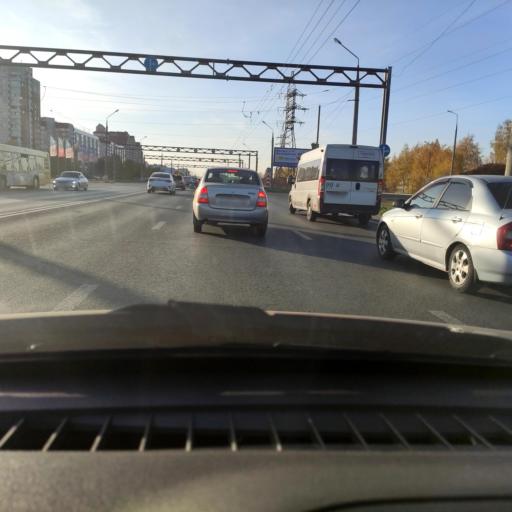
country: RU
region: Samara
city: Tol'yatti
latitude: 53.5457
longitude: 49.3751
